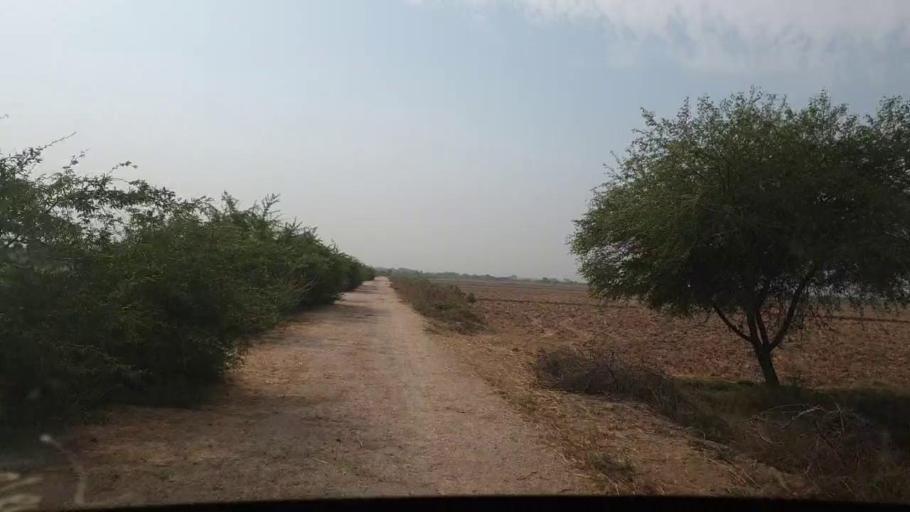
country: PK
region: Sindh
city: Chuhar Jamali
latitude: 24.4116
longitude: 67.9385
